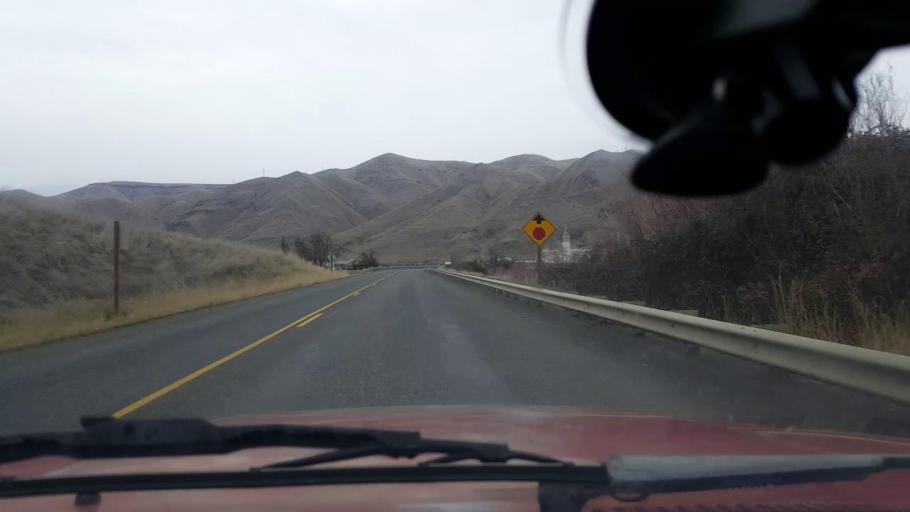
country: US
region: Washington
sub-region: Asotin County
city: Clarkston Heights-Vineland
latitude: 46.4175
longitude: -117.1142
